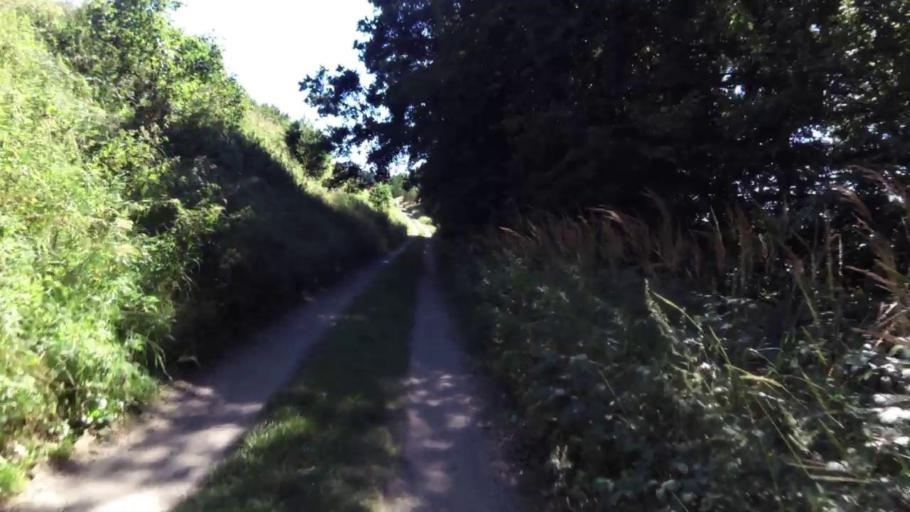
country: PL
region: West Pomeranian Voivodeship
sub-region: Powiat szczecinecki
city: Bialy Bor
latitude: 53.8425
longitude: 16.8730
